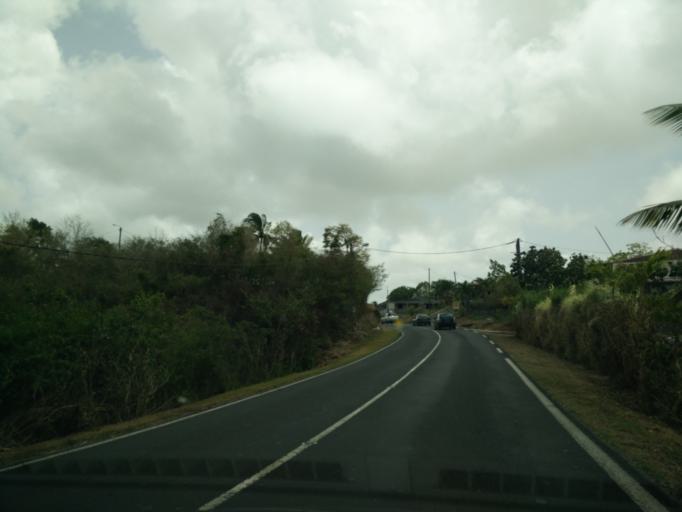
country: GP
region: Guadeloupe
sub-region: Guadeloupe
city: Petit-Canal
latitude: 16.3617
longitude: -61.4559
